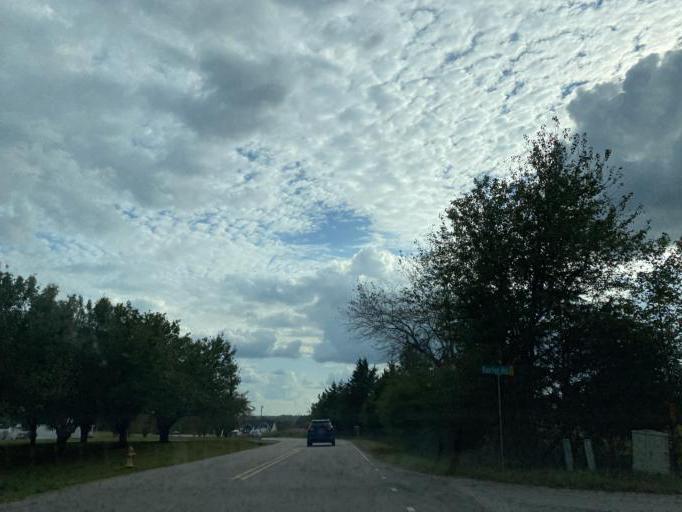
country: US
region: South Carolina
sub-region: Cherokee County
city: Gaffney
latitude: 35.0754
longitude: -81.7130
